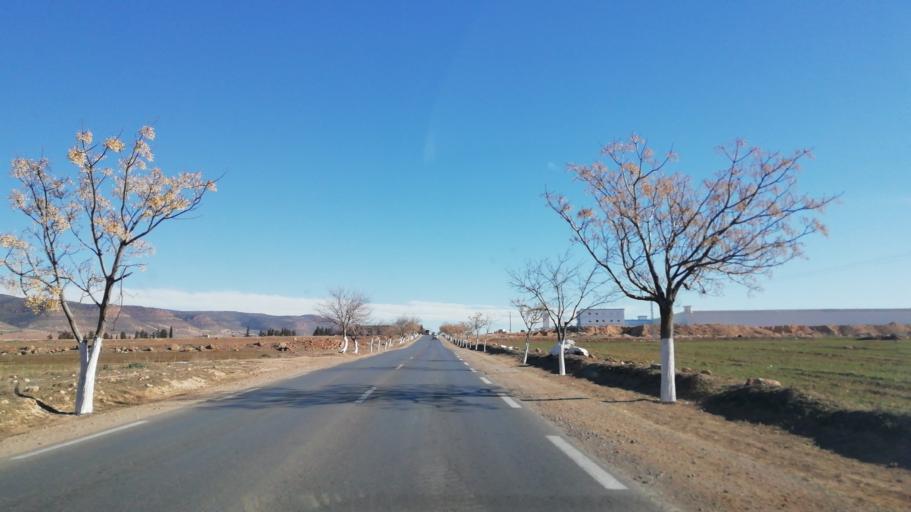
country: DZ
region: Tlemcen
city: Sebdou
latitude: 34.6594
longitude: -1.2983
